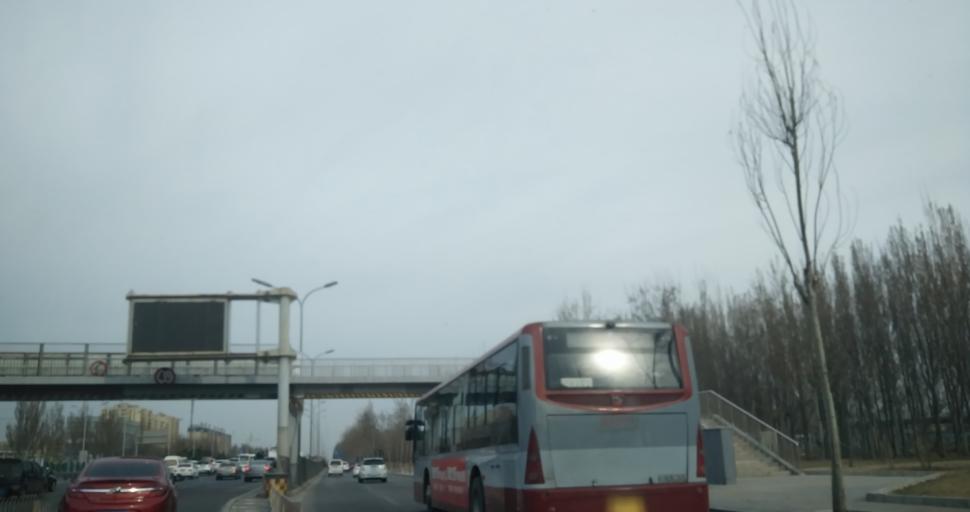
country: CN
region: Beijing
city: Dahongmen
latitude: 39.8298
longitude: 116.3676
